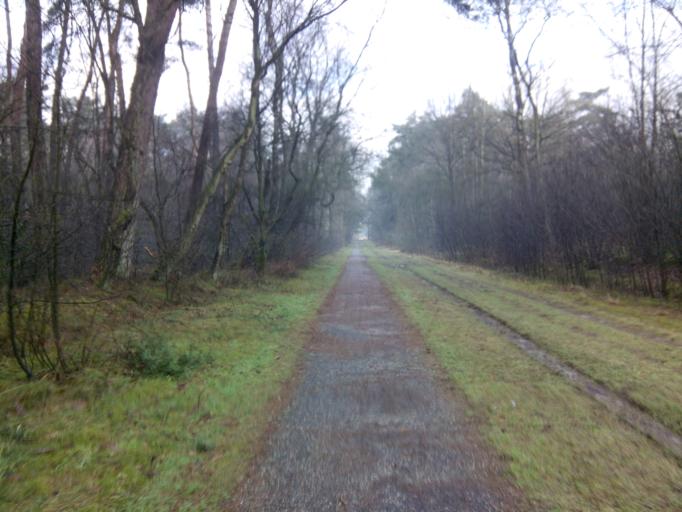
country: NL
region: Utrecht
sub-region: Gemeente Utrechtse Heuvelrug
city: Overberg
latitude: 52.0091
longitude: 5.5016
